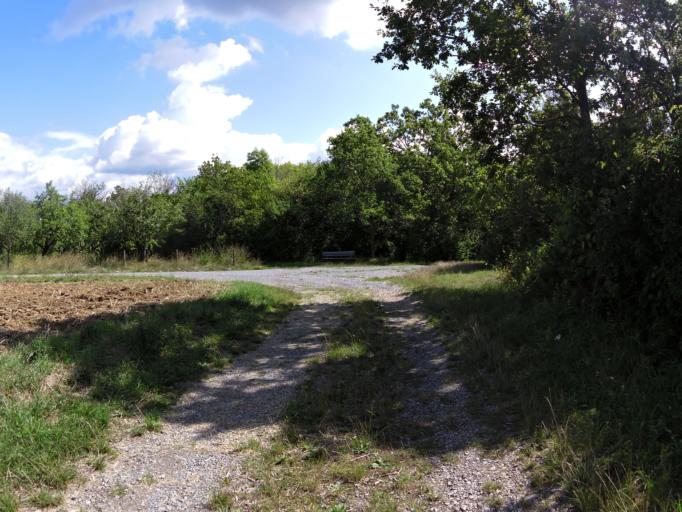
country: DE
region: Bavaria
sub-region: Regierungsbezirk Unterfranken
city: Margetshochheim
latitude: 49.8297
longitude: 9.8586
